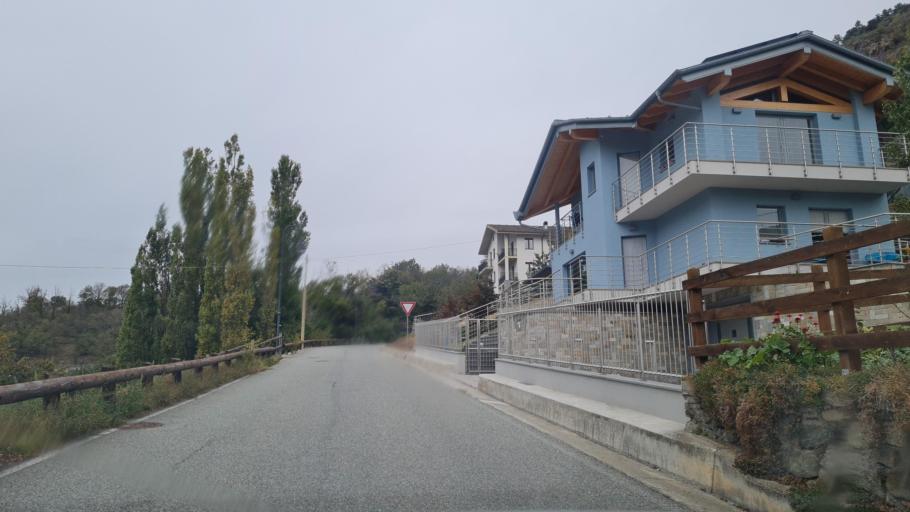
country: IT
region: Aosta Valley
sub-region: Valle d'Aosta
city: Quart
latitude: 45.7474
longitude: 7.4043
